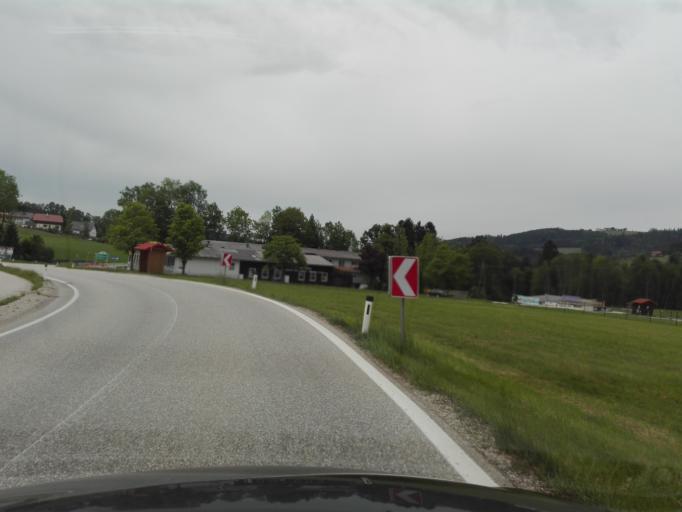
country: AT
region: Upper Austria
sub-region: Politischer Bezirk Gmunden
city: Scharnstein
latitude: 47.9102
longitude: 13.9051
